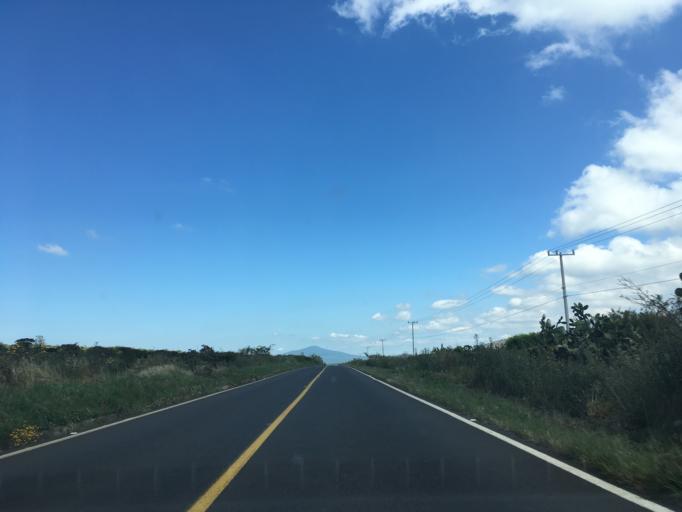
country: MX
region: Michoacan
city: Churintzio
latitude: 20.0987
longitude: -102.0620
